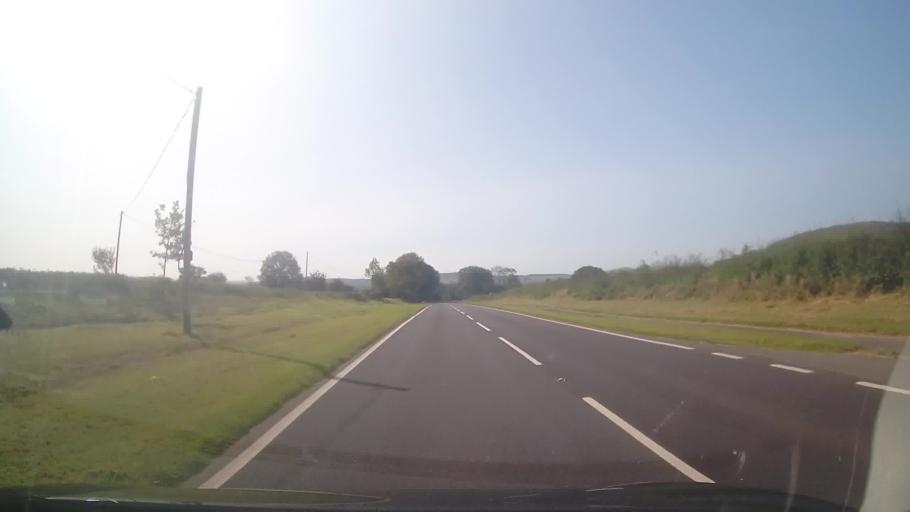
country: GB
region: Wales
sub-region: Carmarthenshire
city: Llandovery
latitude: 52.1132
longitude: -3.6318
